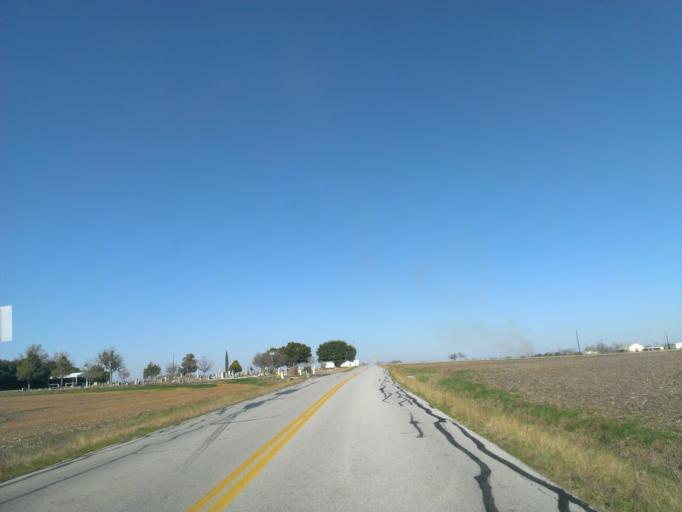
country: US
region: Texas
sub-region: Williamson County
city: Georgetown
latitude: 30.6607
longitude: -97.5819
